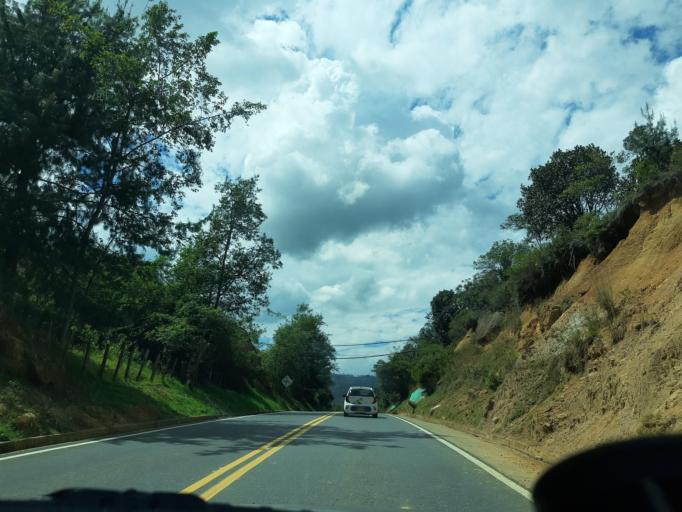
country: CO
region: Boyaca
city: Sutamarchan
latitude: 5.5900
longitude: -73.6902
